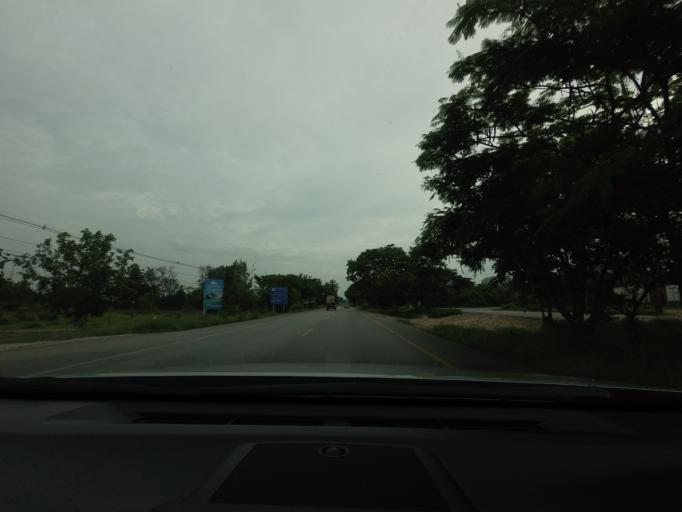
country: TH
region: Phetchaburi
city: Cha-am
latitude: 12.7232
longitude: 99.9233
